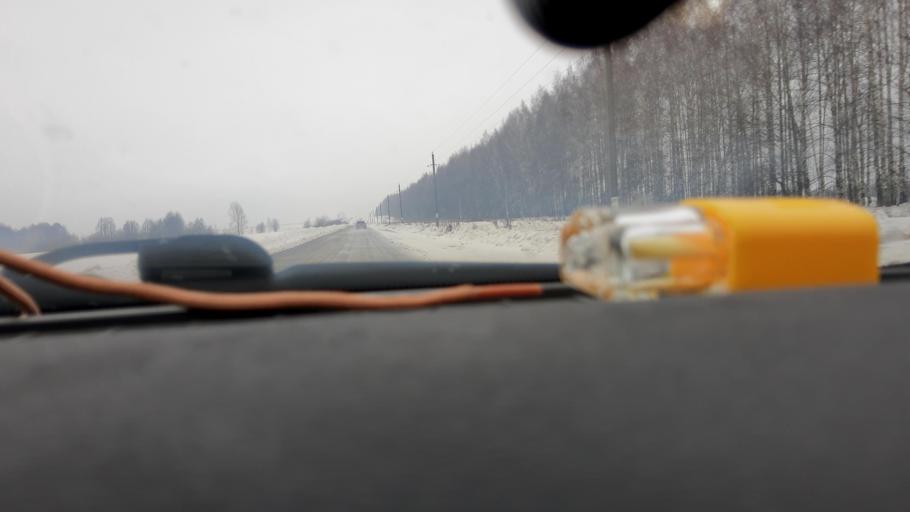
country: RU
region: Bashkortostan
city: Ulukulevo
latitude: 54.5745
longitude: 56.4286
